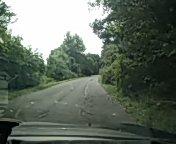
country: HU
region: Hajdu-Bihar
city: Hajdusamson
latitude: 47.5034
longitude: 21.7373
